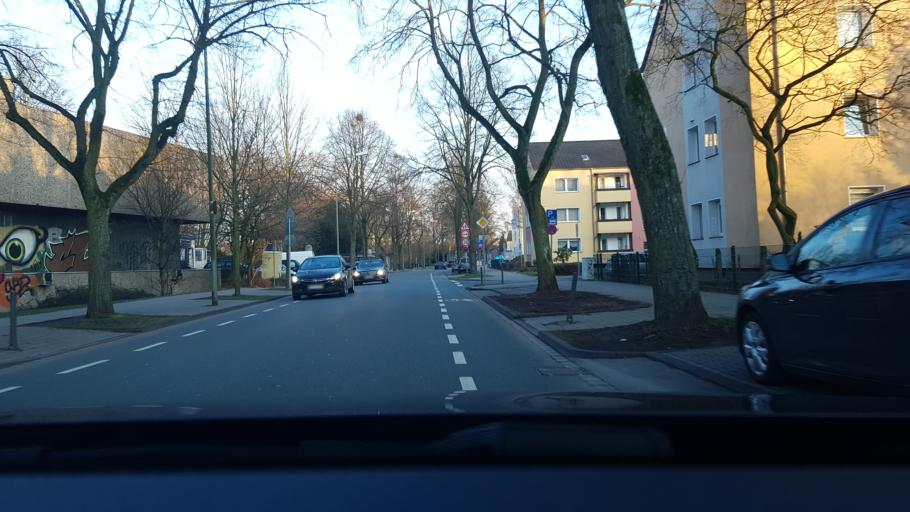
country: DE
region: North Rhine-Westphalia
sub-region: Regierungsbezirk Dusseldorf
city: Hochfeld
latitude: 51.4080
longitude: 6.6984
